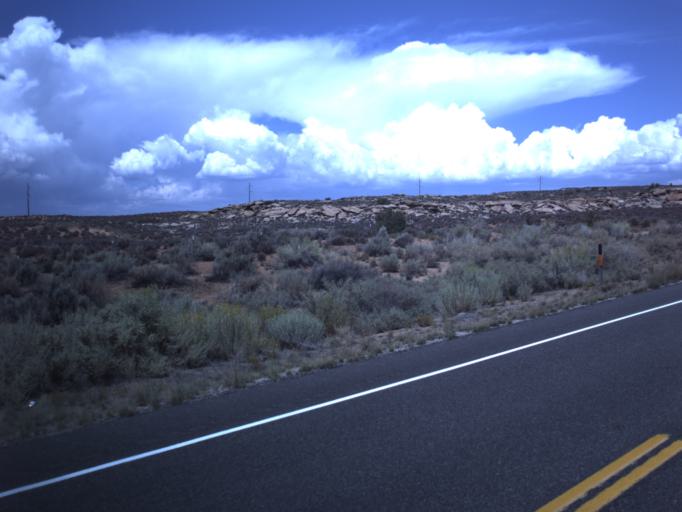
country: US
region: Utah
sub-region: San Juan County
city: Blanding
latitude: 37.3726
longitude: -109.5060
